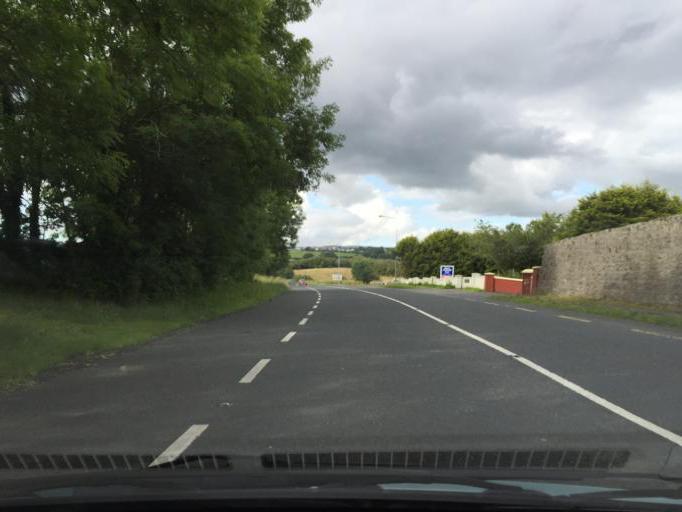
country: IE
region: Connaught
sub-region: Sligo
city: Sligo
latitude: 54.2375
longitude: -8.4783
